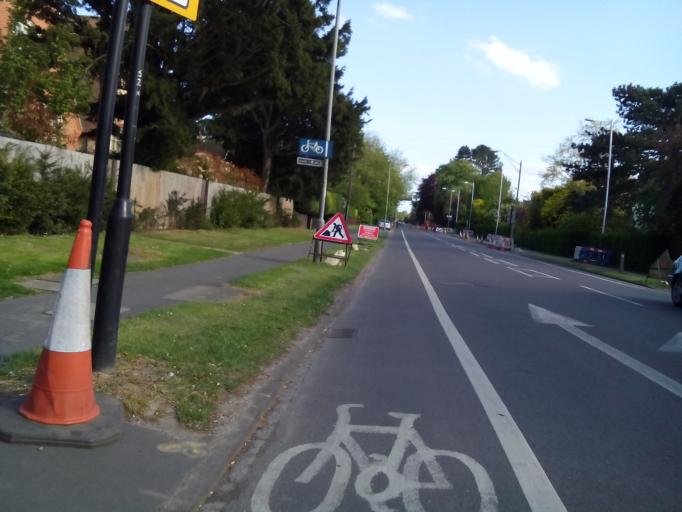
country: GB
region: England
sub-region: Cambridgeshire
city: Cambridge
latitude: 52.1845
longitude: 0.1390
